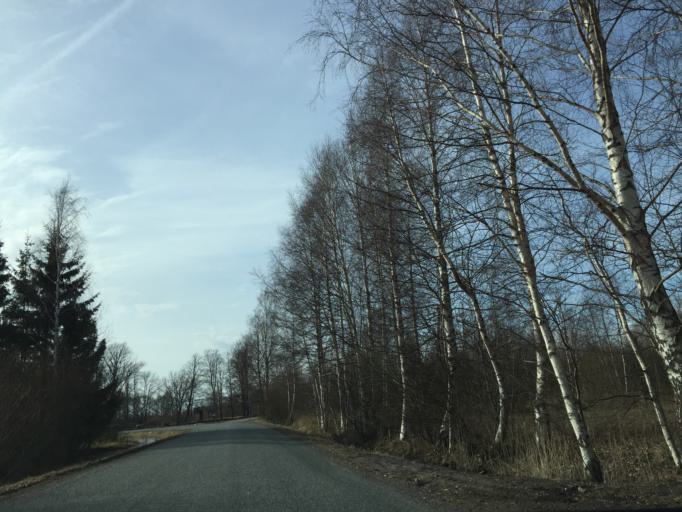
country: EE
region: Paernumaa
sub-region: Paernu linn
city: Parnu
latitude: 58.2464
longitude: 24.5052
